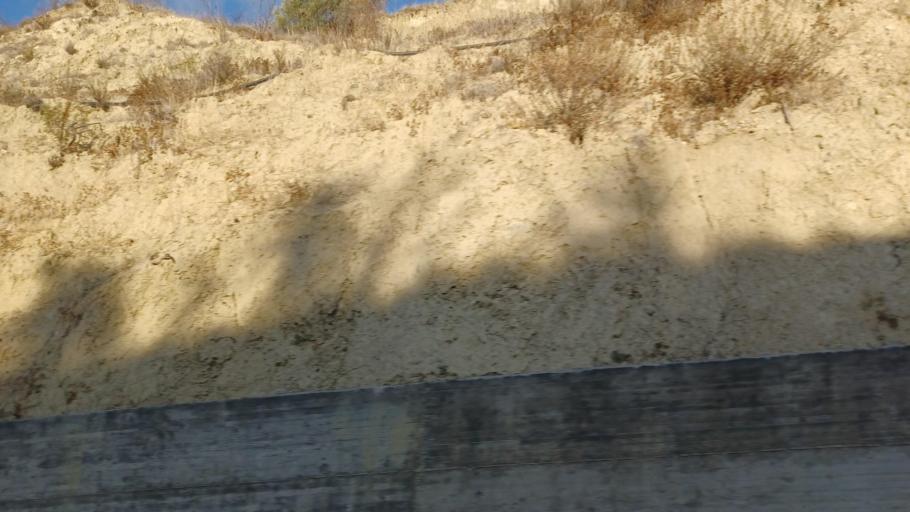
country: CY
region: Limassol
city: Pachna
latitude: 34.8566
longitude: 32.7202
